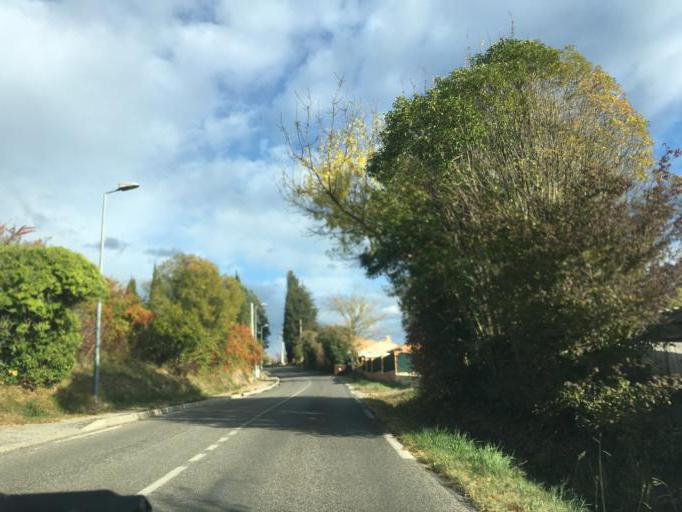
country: FR
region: Provence-Alpes-Cote d'Azur
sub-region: Departement du Var
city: Salernes
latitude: 43.5621
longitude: 6.2464
